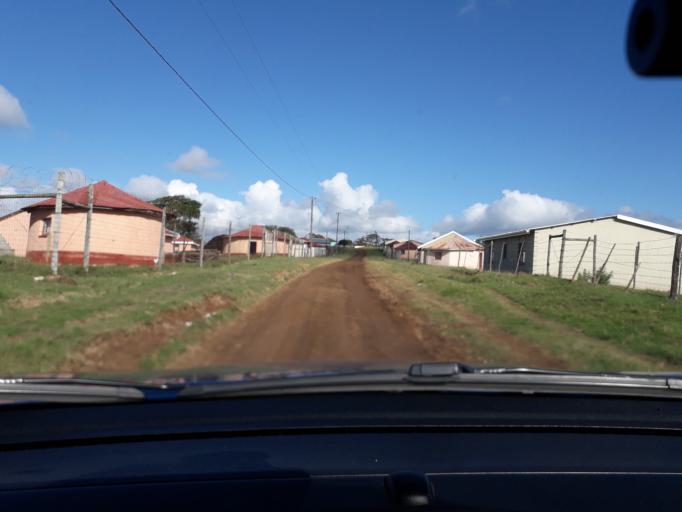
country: ZA
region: Eastern Cape
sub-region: Buffalo City Metropolitan Municipality
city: Bhisho
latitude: -33.1076
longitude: 27.4266
